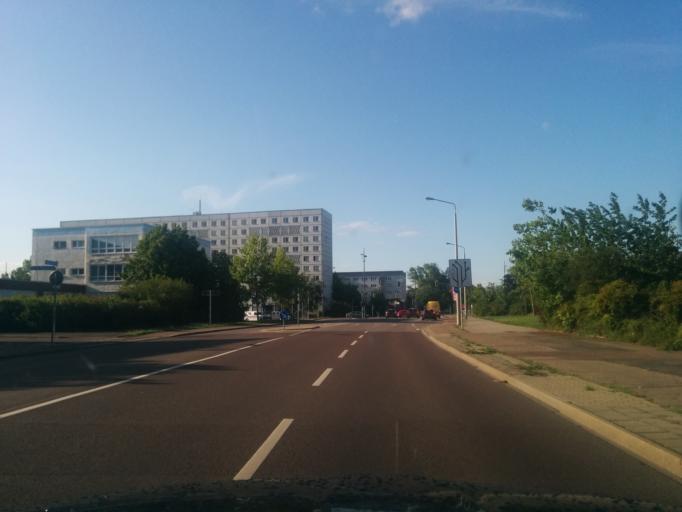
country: DE
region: Saxony-Anhalt
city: Halle Neustadt
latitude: 51.4802
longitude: 11.9117
